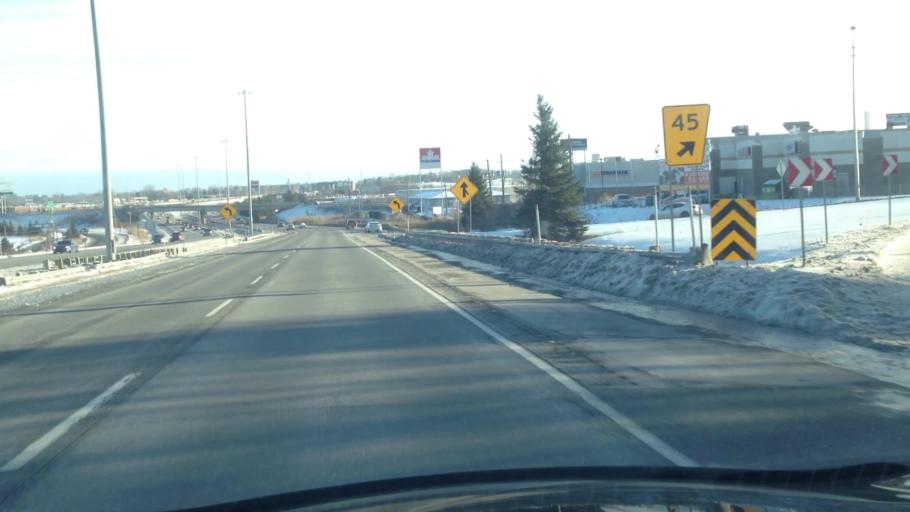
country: CA
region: Quebec
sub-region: Laurentides
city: Saint-Jerome
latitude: 45.7990
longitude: -74.0295
